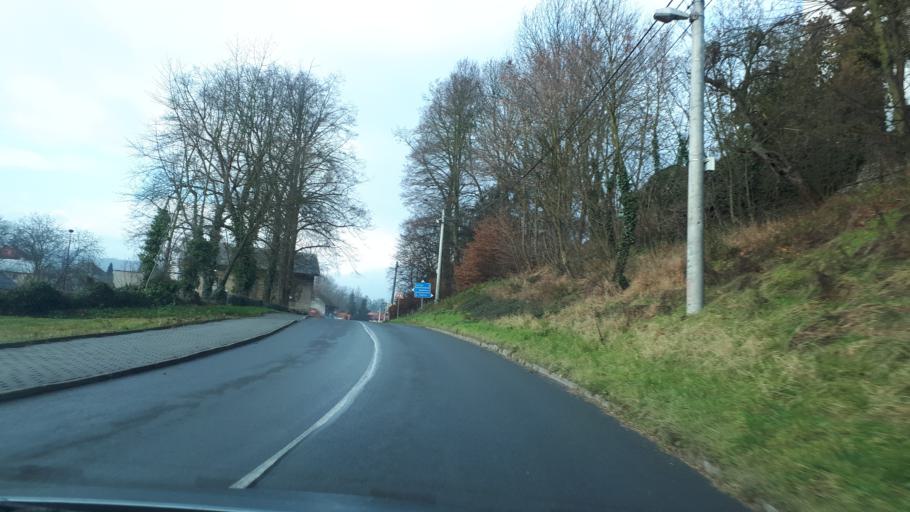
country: CZ
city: Jesenik nad Odrou
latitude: 49.6551
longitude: 17.9300
